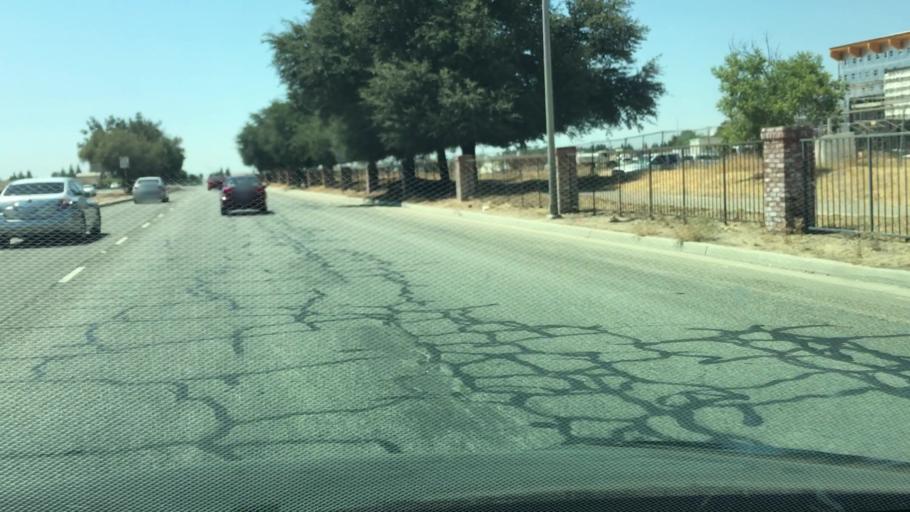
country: US
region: California
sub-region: Fresno County
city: Fresno
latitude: 36.8370
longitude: -119.8631
